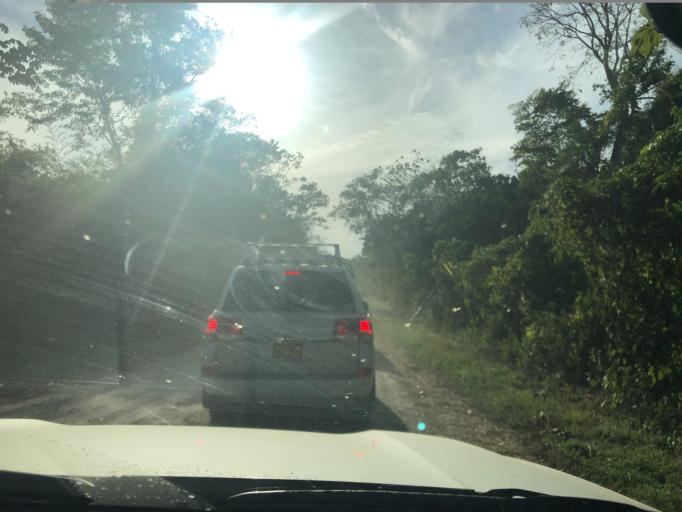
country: NI
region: Rivas
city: Cardenas
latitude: 11.1276
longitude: -85.3068
